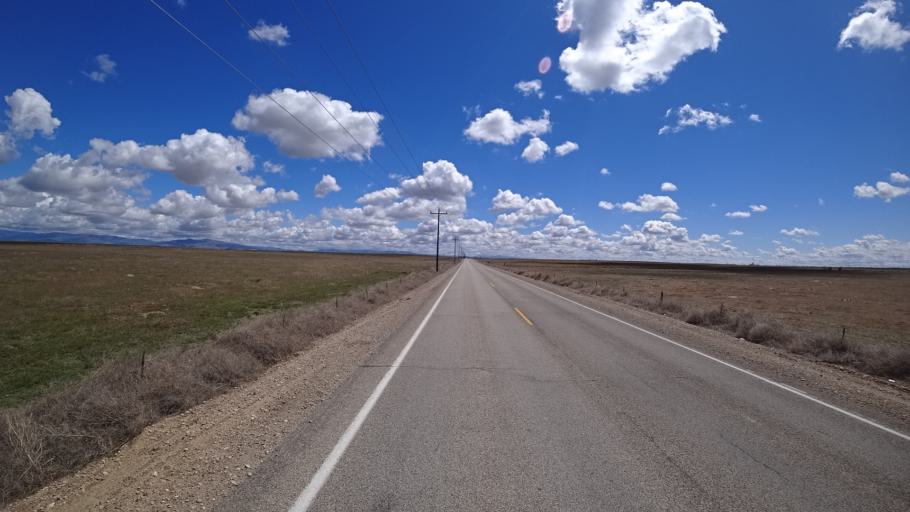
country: US
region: Idaho
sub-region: Ada County
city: Kuna
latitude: 43.4592
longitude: -116.3114
